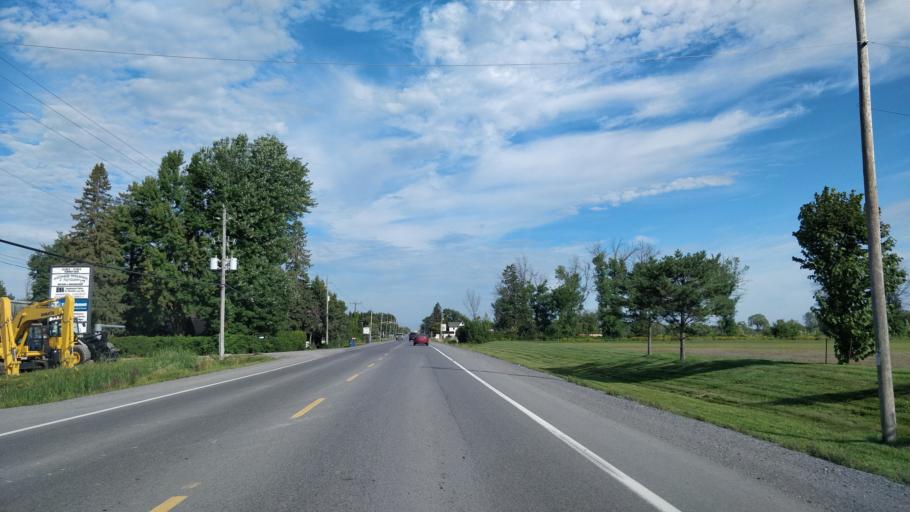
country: CA
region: Ontario
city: Bells Corners
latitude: 45.3044
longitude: -75.9859
